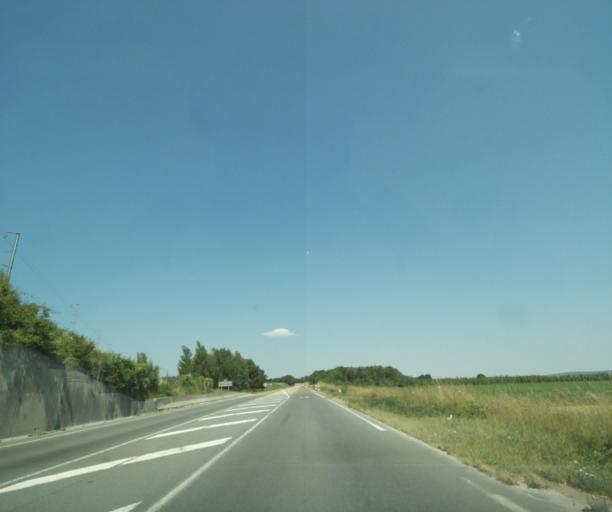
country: FR
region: Champagne-Ardenne
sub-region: Departement de la Marne
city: Verzy
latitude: 49.1106
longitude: 4.2565
